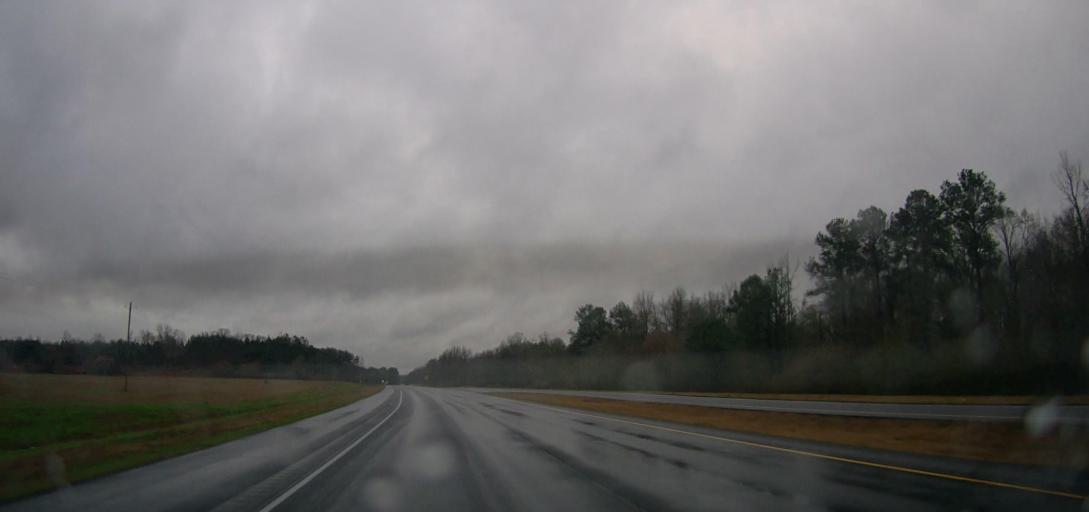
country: US
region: Alabama
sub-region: Bibb County
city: Centreville
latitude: 32.9333
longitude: -87.0597
